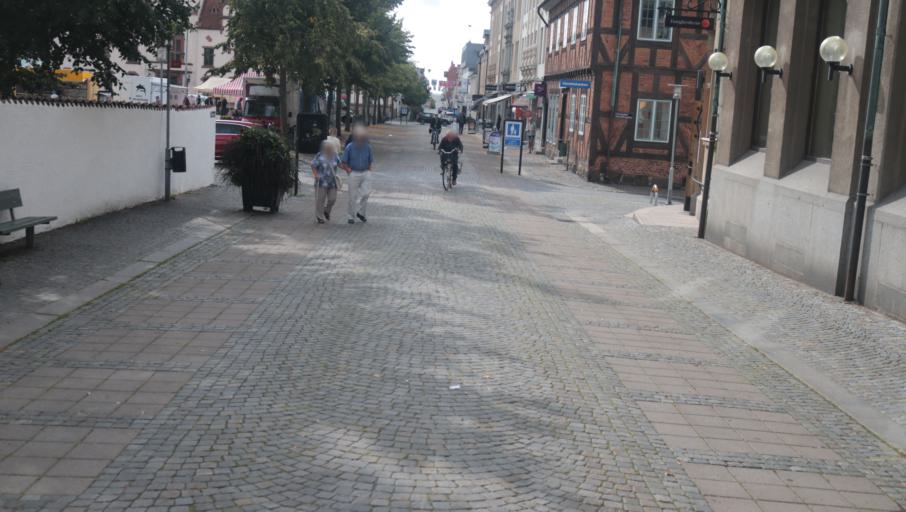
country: SE
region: Blekinge
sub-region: Karlshamns Kommun
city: Karlshamn
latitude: 56.1711
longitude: 14.8616
